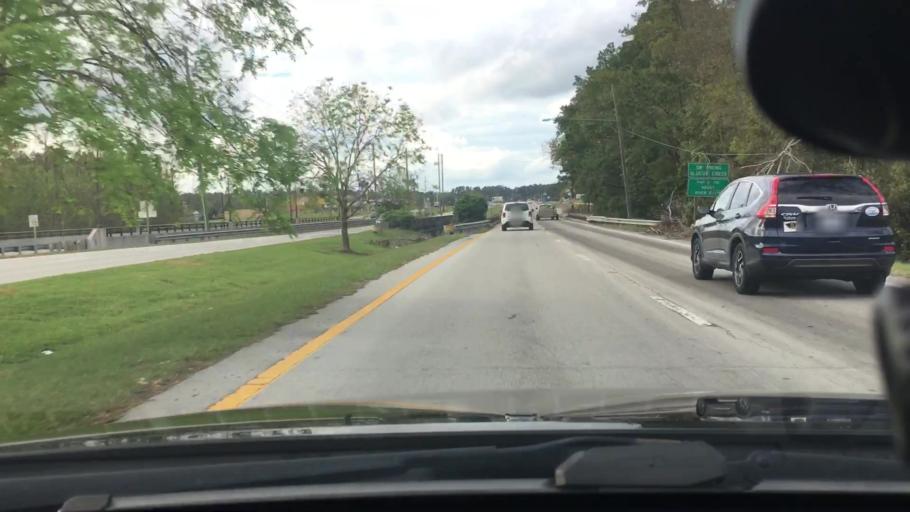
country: US
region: North Carolina
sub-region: Craven County
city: Havelock
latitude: 34.8906
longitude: -76.9220
